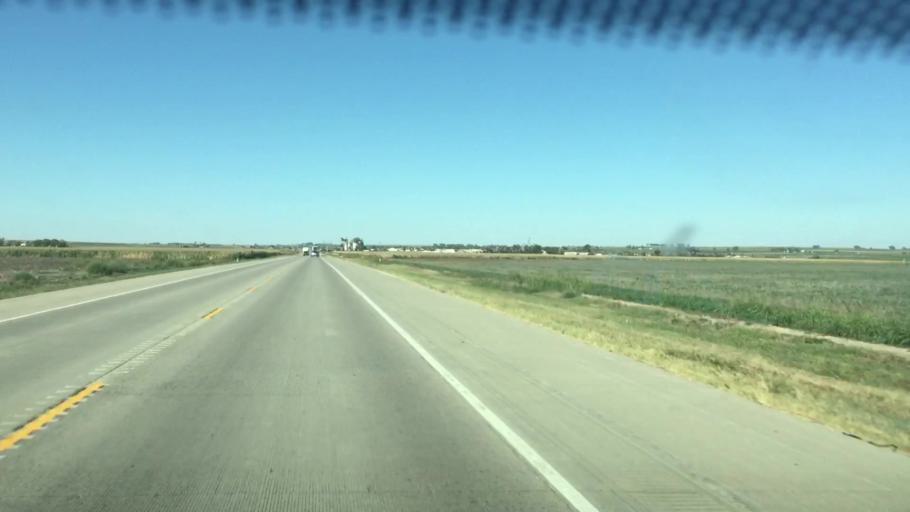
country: US
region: Colorado
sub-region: Prowers County
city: Lamar
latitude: 38.1312
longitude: -102.7237
